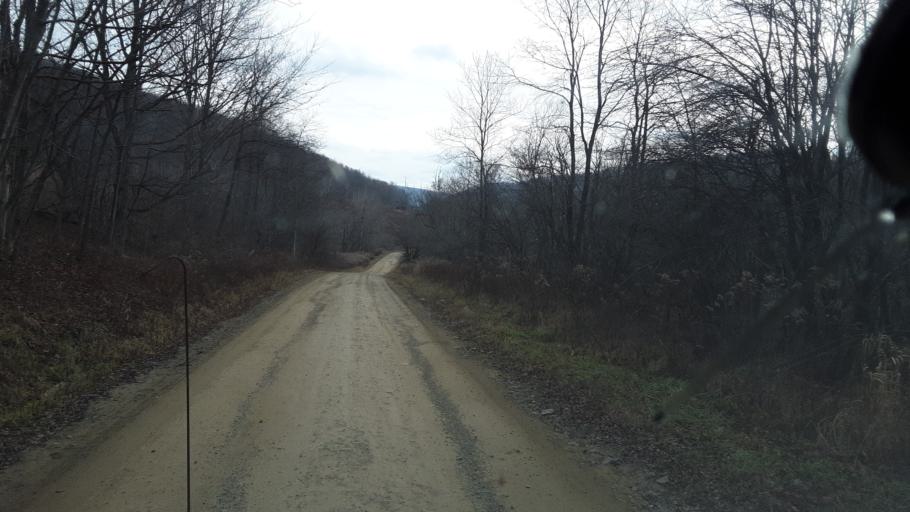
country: US
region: Pennsylvania
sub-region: Tioga County
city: Westfield
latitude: 41.9050
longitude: -77.7159
